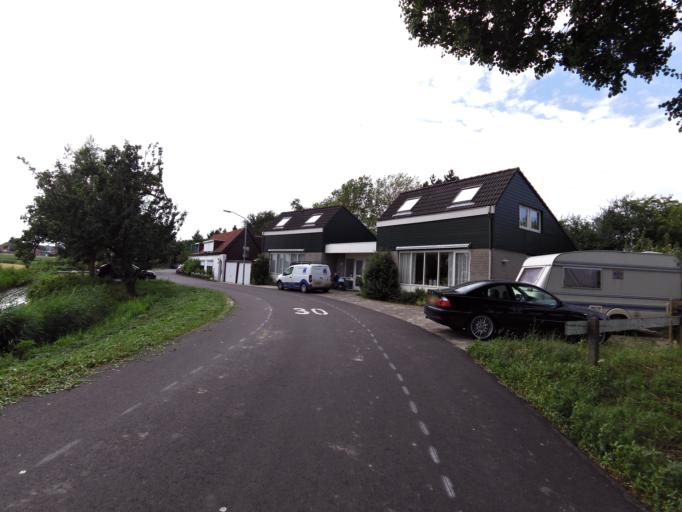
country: NL
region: South Holland
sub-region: Gemeente Dordrecht
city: Dordrecht
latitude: 51.7887
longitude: 4.7008
